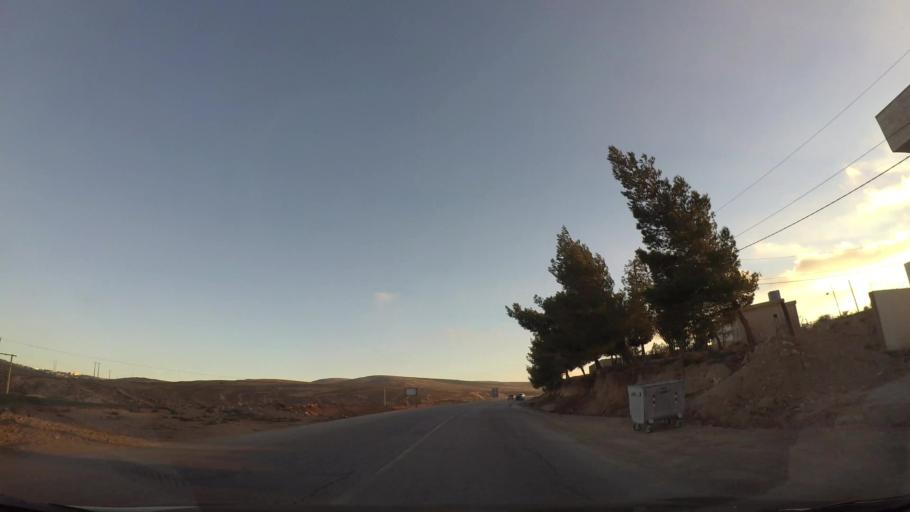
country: JO
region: Ma'an
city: Petra
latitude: 30.4514
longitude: 35.5254
